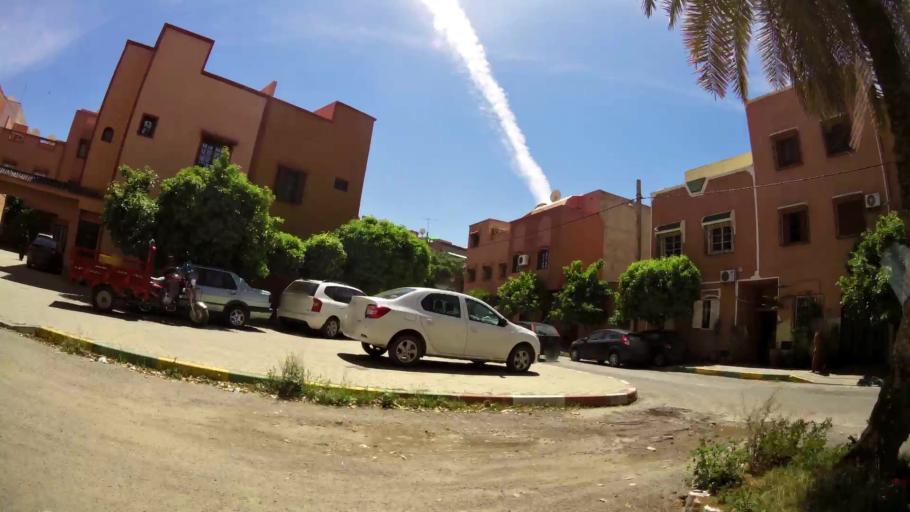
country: MA
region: Marrakech-Tensift-Al Haouz
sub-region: Marrakech
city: Marrakesh
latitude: 31.6400
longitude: -8.0512
